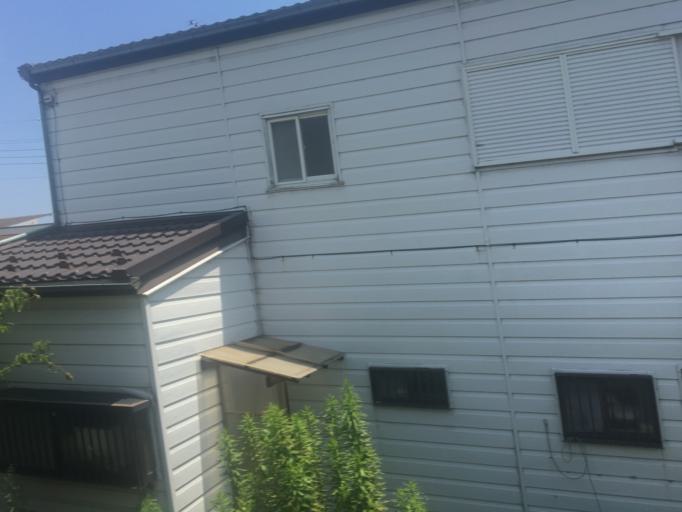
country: JP
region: Saitama
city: Yorii
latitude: 36.1278
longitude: 139.2032
